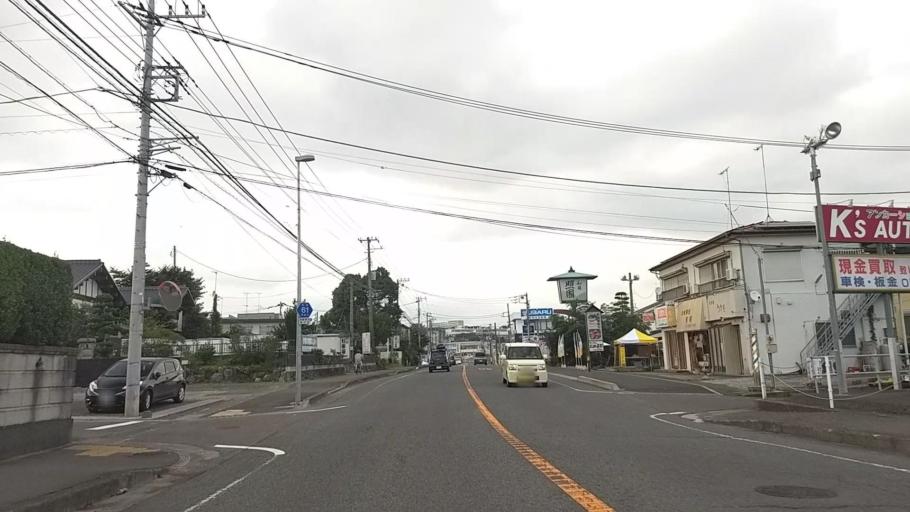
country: JP
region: Kanagawa
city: Isehara
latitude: 35.3837
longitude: 139.3162
